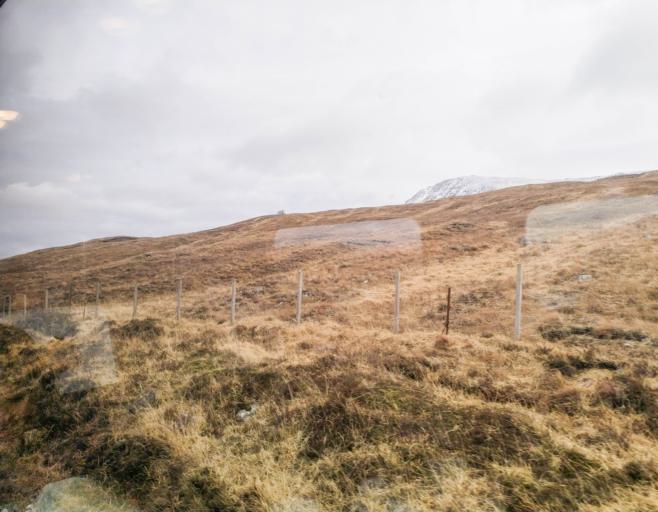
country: GB
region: Scotland
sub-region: Highland
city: Spean Bridge
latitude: 56.5463
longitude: -4.7539
